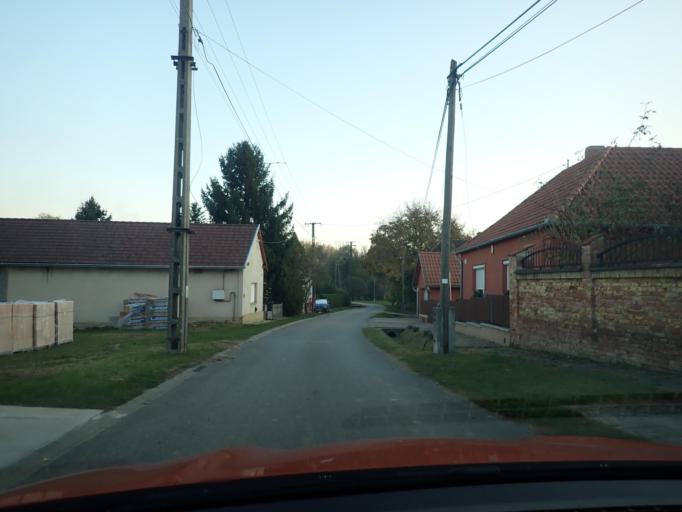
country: HU
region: Baranya
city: Kozarmisleny
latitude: 46.0318
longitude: 18.3880
